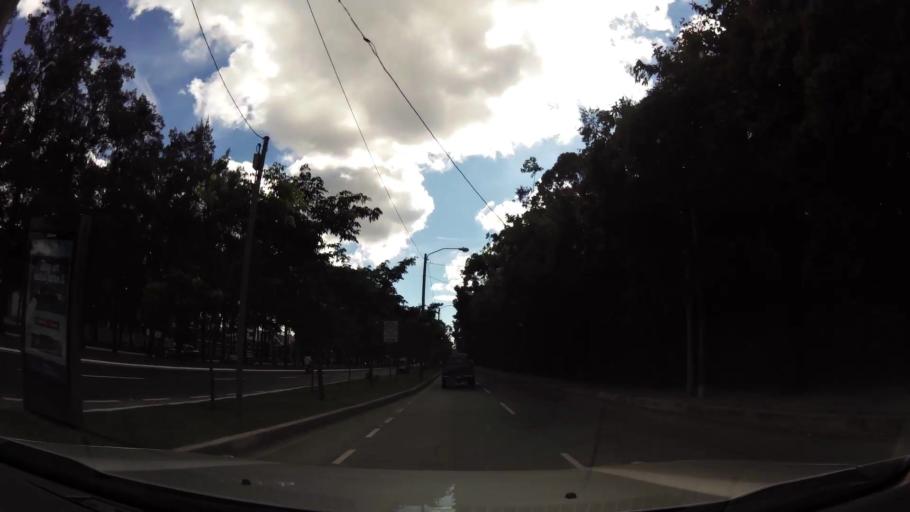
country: GT
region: Guatemala
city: Mixco
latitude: 14.6062
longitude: -90.5592
